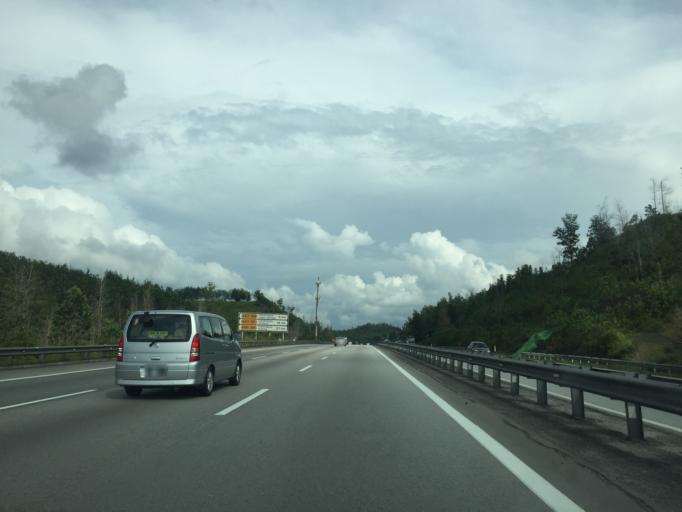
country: MY
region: Selangor
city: Batang Berjuntai
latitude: 3.5314
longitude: 101.5216
